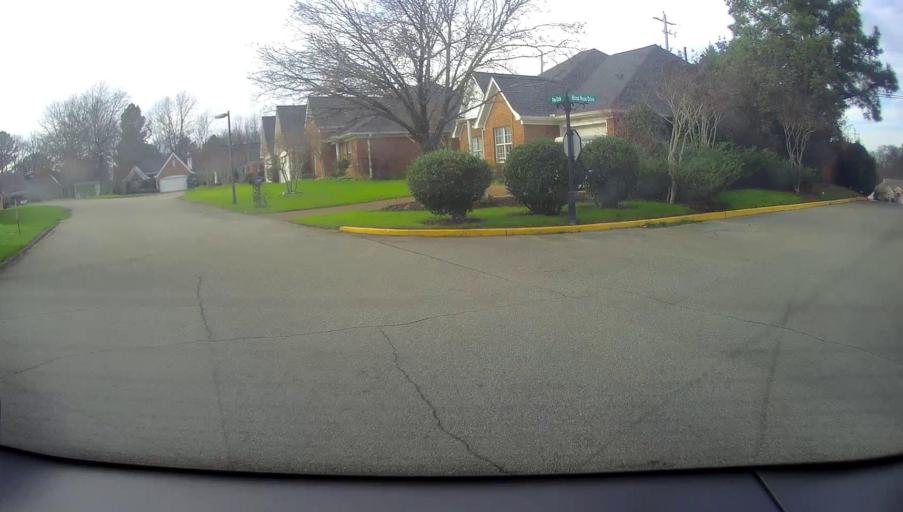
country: US
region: Tennessee
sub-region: Shelby County
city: Germantown
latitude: 35.0580
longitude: -89.8517
